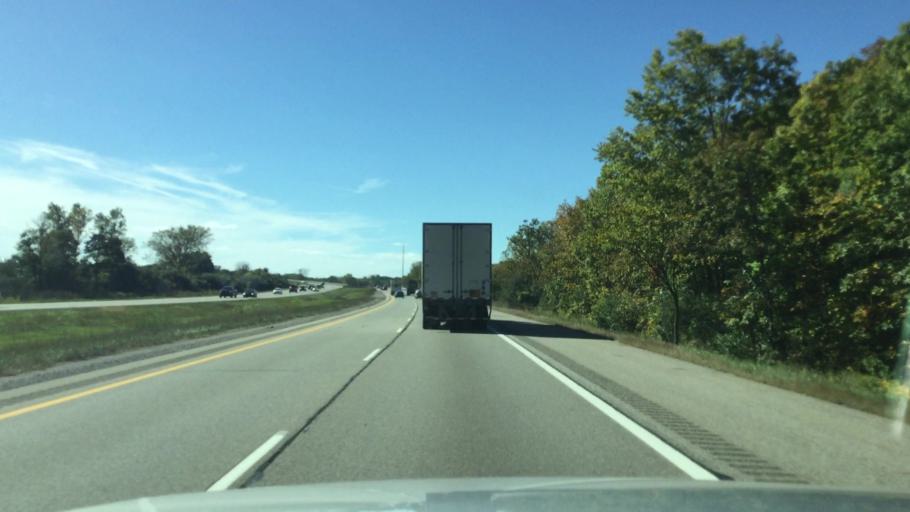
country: US
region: Michigan
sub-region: Washtenaw County
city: Ann Arbor
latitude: 42.3253
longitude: -83.6775
